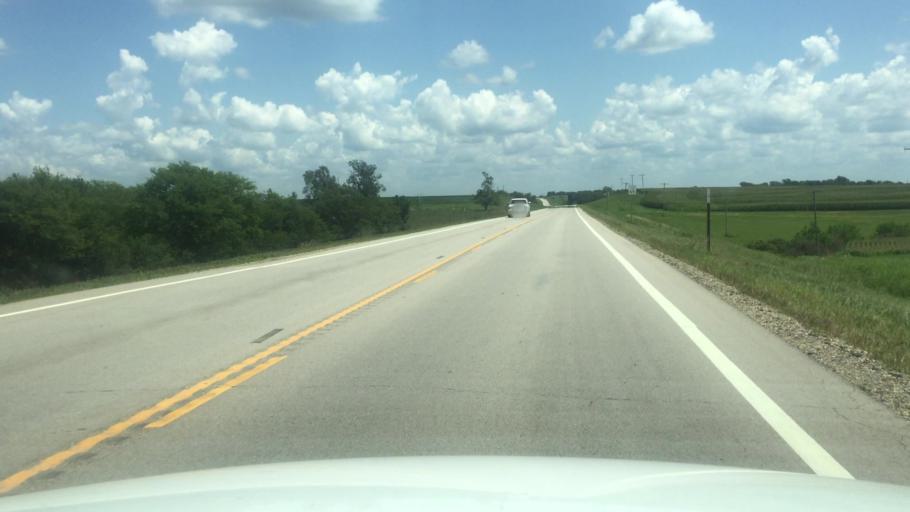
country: US
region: Kansas
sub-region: Brown County
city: Horton
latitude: 39.6676
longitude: -95.4878
